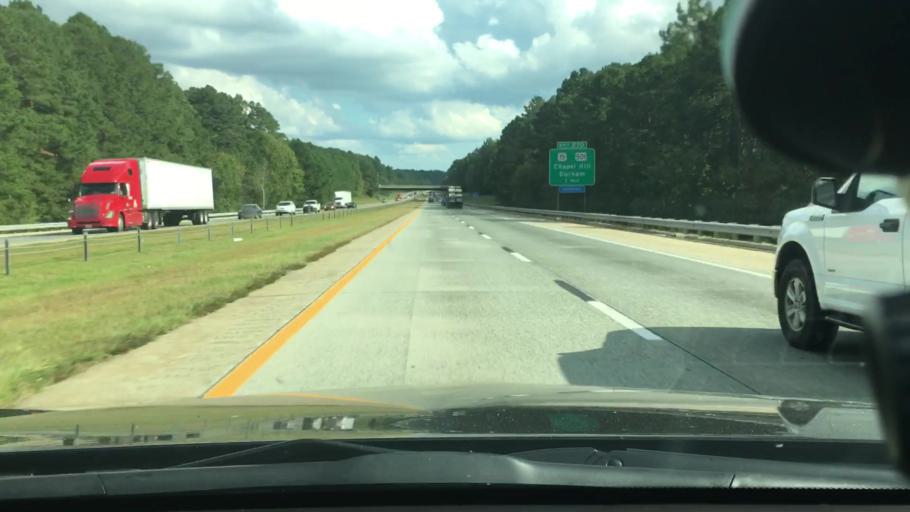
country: US
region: North Carolina
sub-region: Orange County
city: Chapel Hill
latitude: 35.9624
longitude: -79.0172
